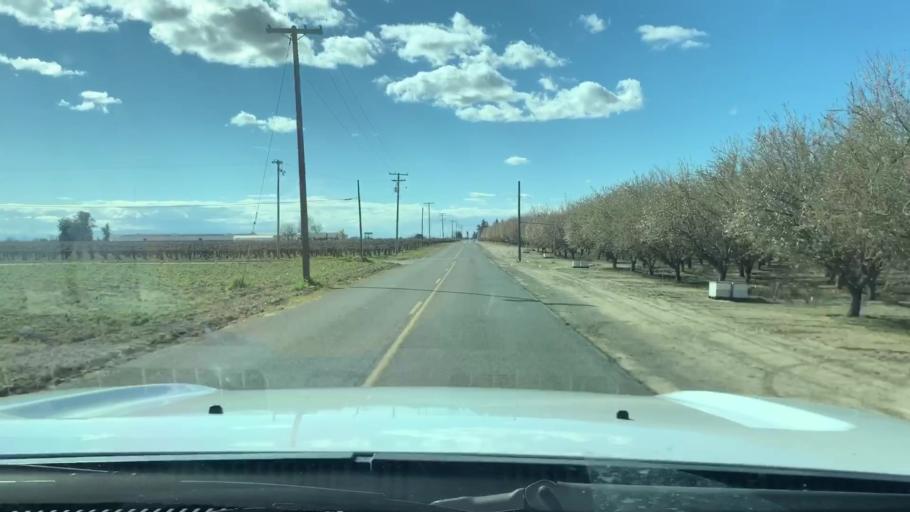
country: US
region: California
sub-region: Fresno County
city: Fowler
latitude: 36.5619
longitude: -119.7283
